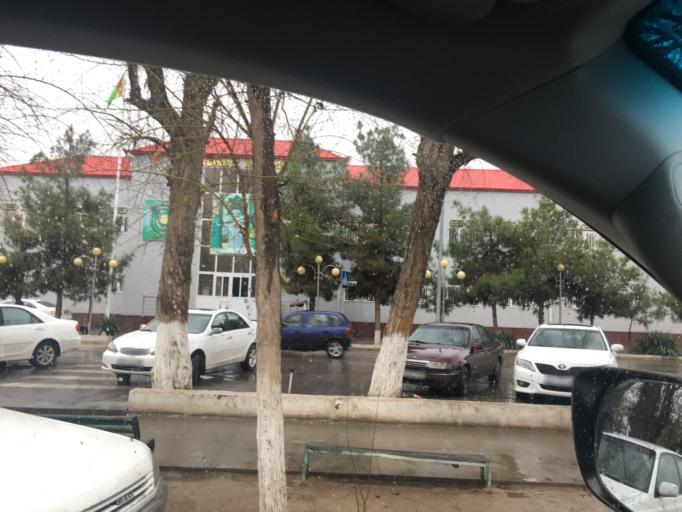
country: TM
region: Mary
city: Yoloeten
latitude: 37.2999
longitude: 62.3588
